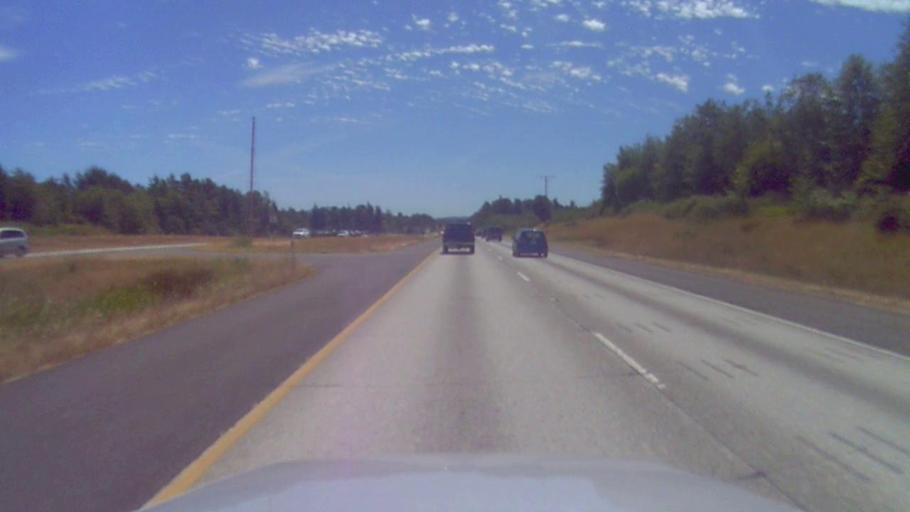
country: US
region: Washington
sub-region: Whatcom County
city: Marietta-Alderwood
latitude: 48.8062
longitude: -122.5378
